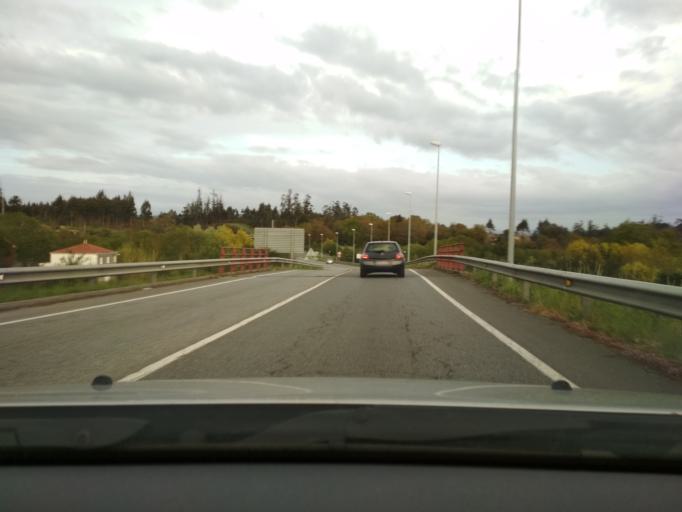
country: ES
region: Galicia
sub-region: Provincia da Coruna
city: Santiago de Compostela
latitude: 42.8985
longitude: -8.5256
